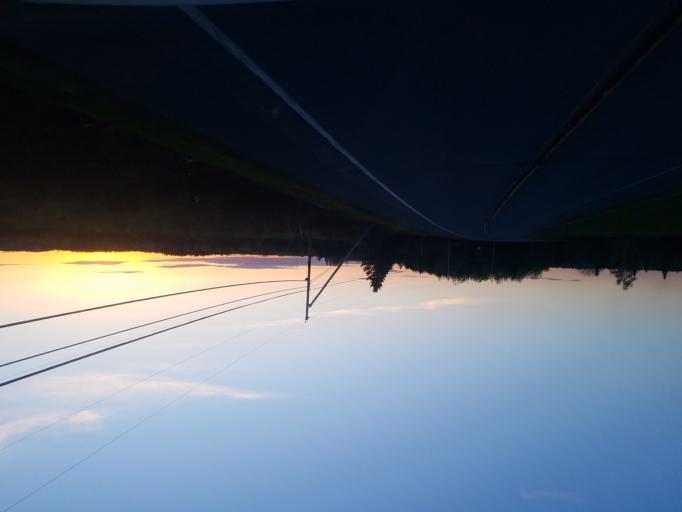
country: US
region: Maine
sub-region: Aroostook County
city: Caribou
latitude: 46.8443
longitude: -68.0599
